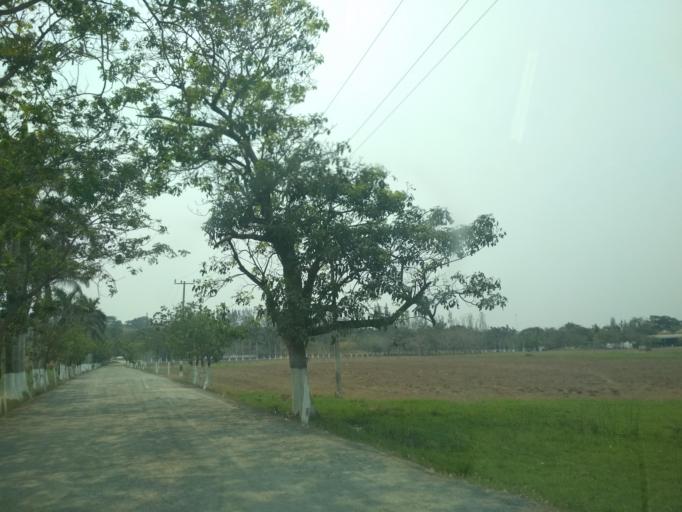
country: MX
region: Veracruz
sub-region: Veracruz
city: Las Amapolas
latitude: 19.1689
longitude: -96.2102
